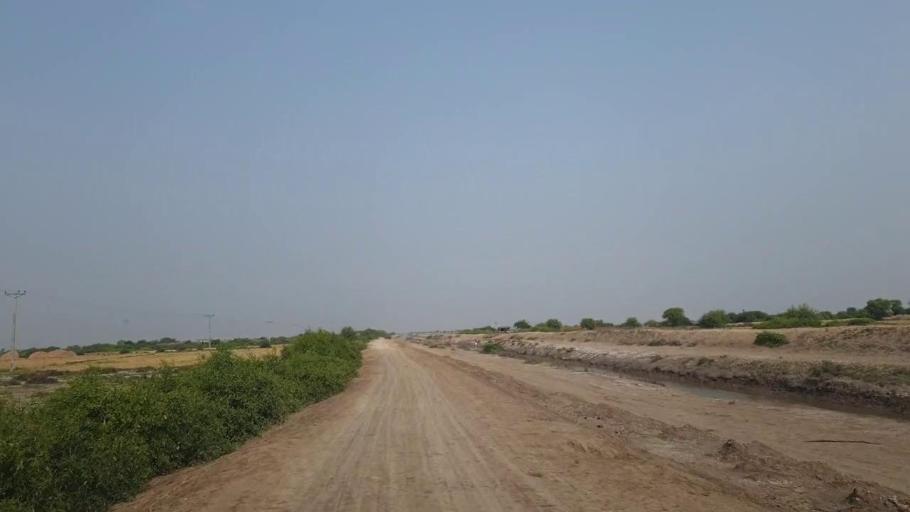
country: PK
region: Sindh
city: Badin
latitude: 24.7129
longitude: 68.7726
